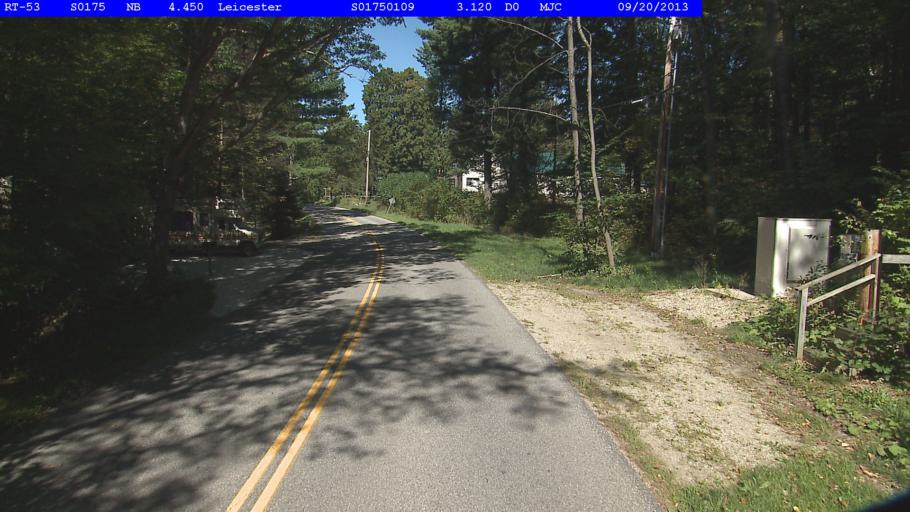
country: US
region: Vermont
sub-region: Rutland County
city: Brandon
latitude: 43.8875
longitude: -73.0642
